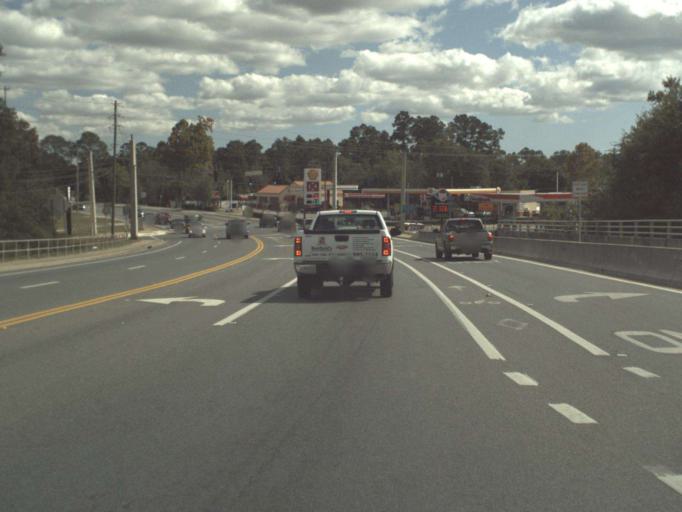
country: US
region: Florida
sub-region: Santa Rosa County
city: East Milton
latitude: 30.6252
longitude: -87.0222
